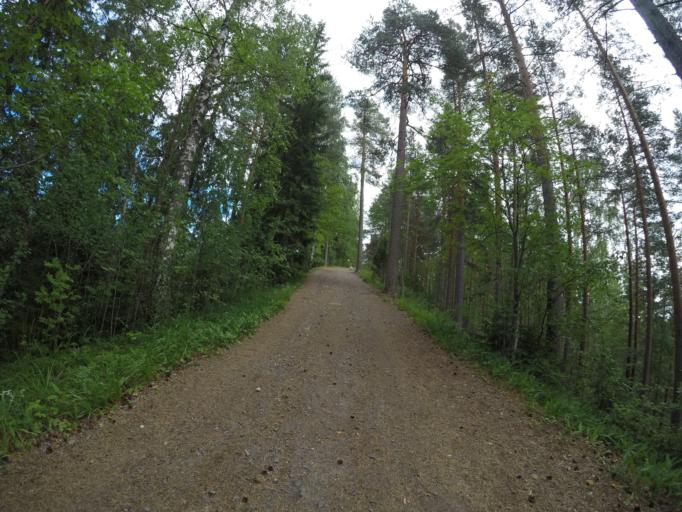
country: FI
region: Haeme
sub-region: Haemeenlinna
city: Haemeenlinna
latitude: 60.9984
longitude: 24.4167
